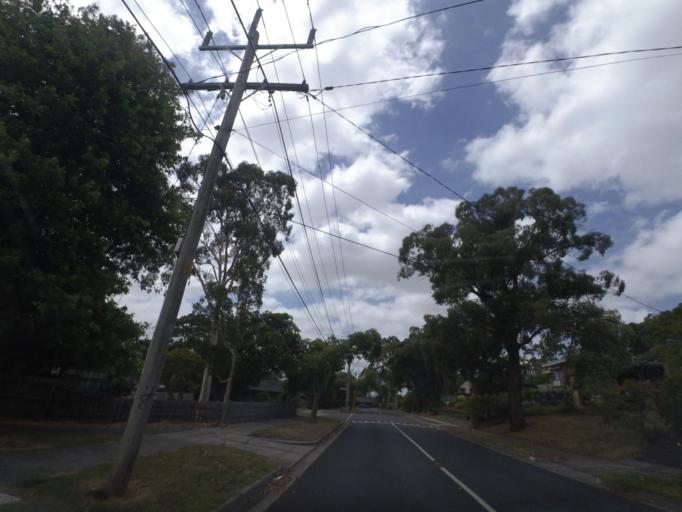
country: AU
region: Victoria
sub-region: Maroondah
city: Croydon South
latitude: -37.8111
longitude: 145.2827
